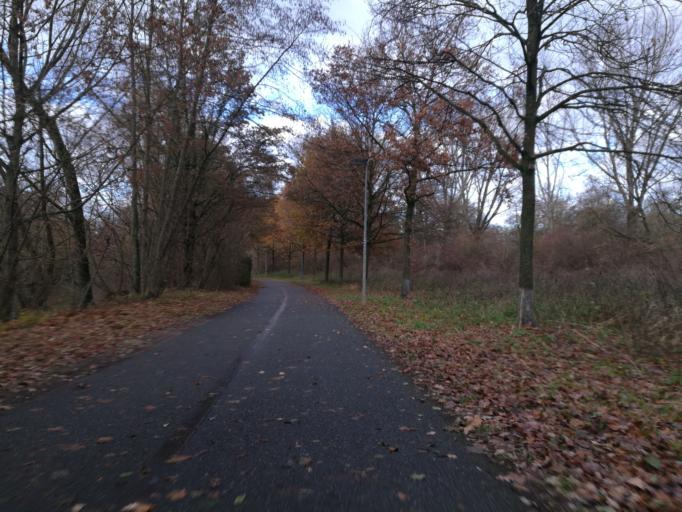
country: DE
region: Bavaria
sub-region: Regierungsbezirk Mittelfranken
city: Furth
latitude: 49.4823
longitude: 10.9929
